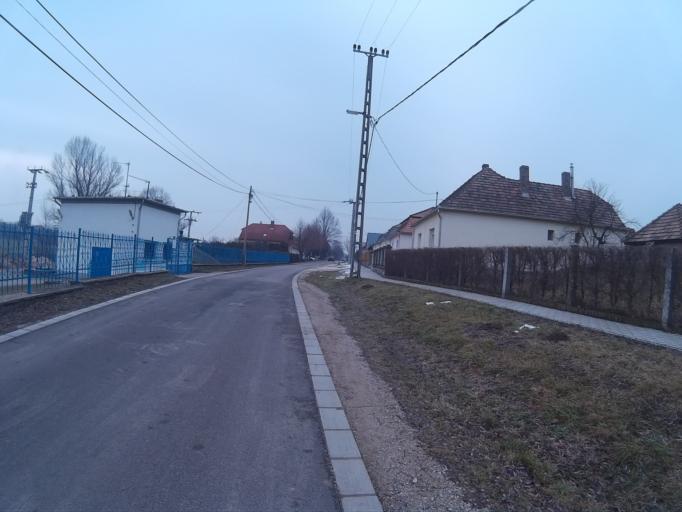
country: HU
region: Komarom-Esztergom
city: Tarjan
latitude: 47.6075
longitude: 18.5094
